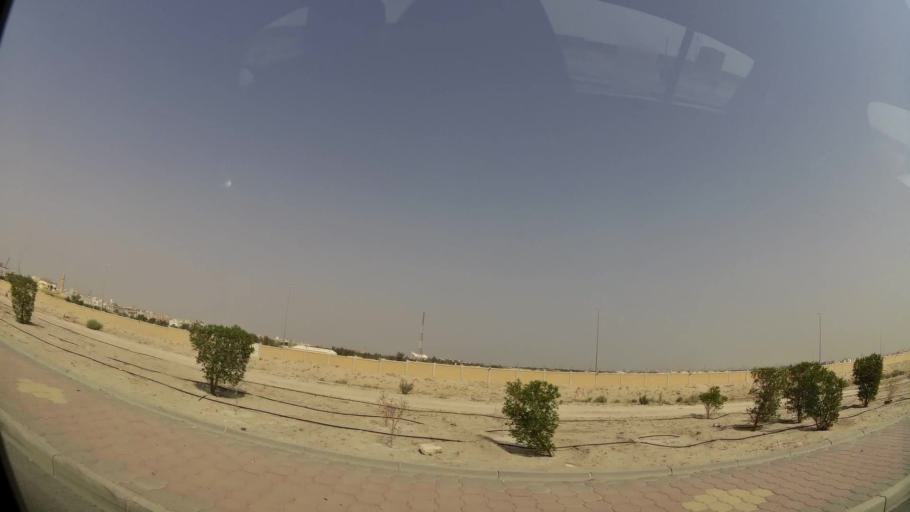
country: KW
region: Muhafazat al Jahra'
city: Al Jahra'
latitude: 29.3242
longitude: 47.7044
